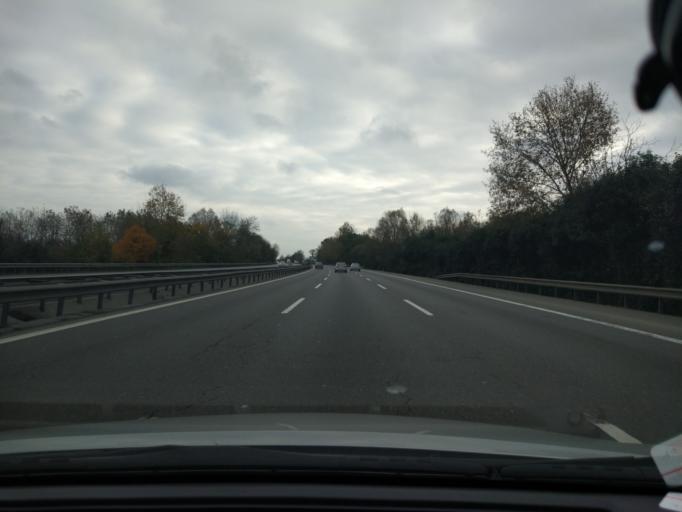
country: TR
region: Kocaeli
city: Derbent
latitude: 40.7115
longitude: 30.1240
